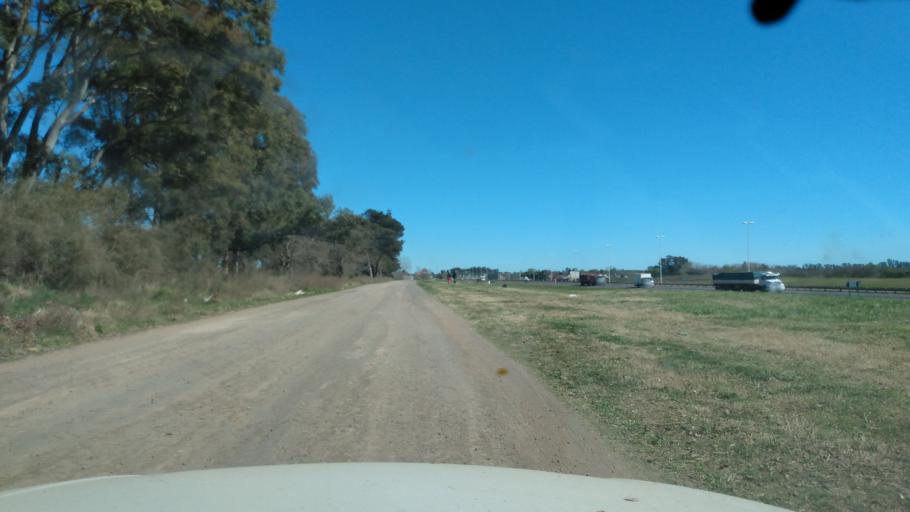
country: AR
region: Buenos Aires
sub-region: Partido de Lujan
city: Lujan
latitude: -34.5666
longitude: -59.0727
